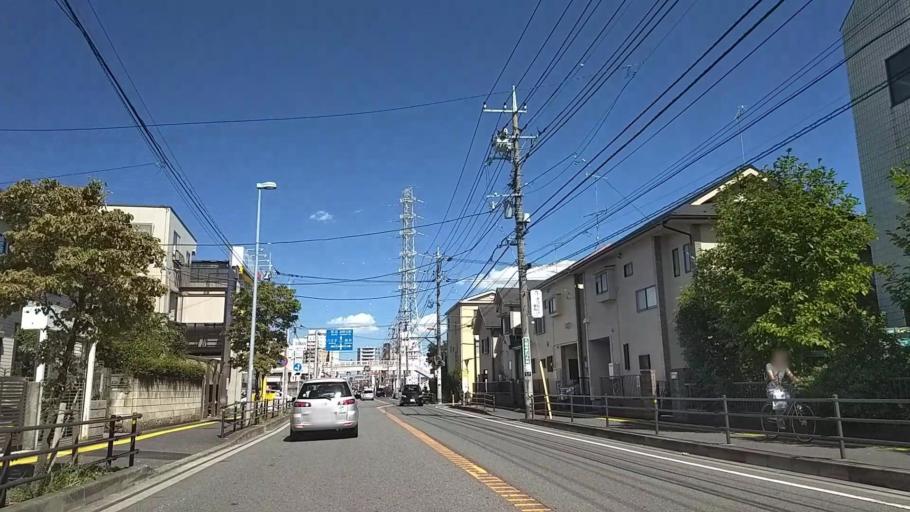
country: JP
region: Tokyo
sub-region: Machida-shi
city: Machida
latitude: 35.5636
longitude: 139.3910
